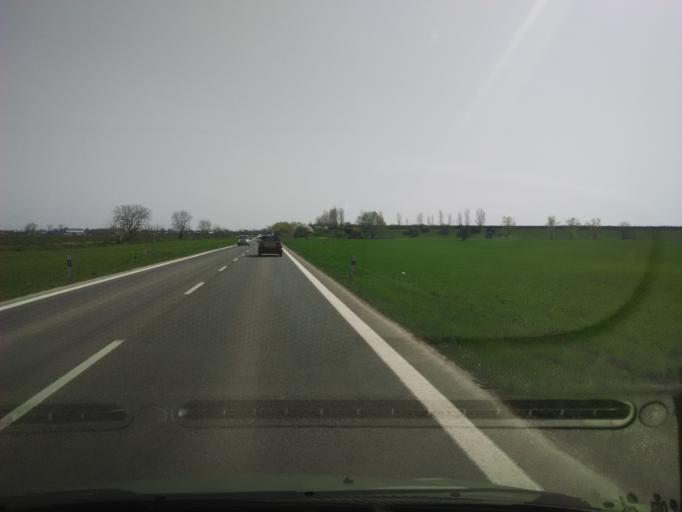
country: SK
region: Nitriansky
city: Sellye
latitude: 48.1601
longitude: 17.9080
